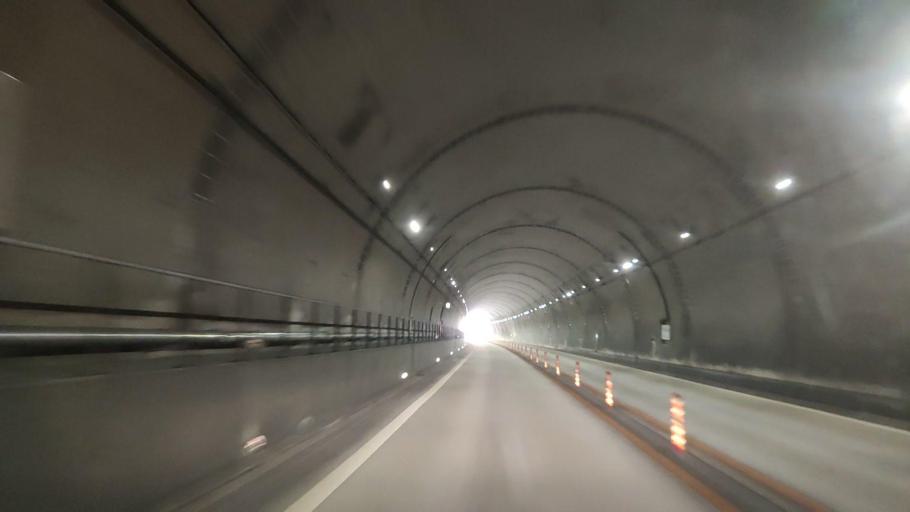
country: JP
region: Ehime
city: Hojo
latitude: 34.0857
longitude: 132.9780
